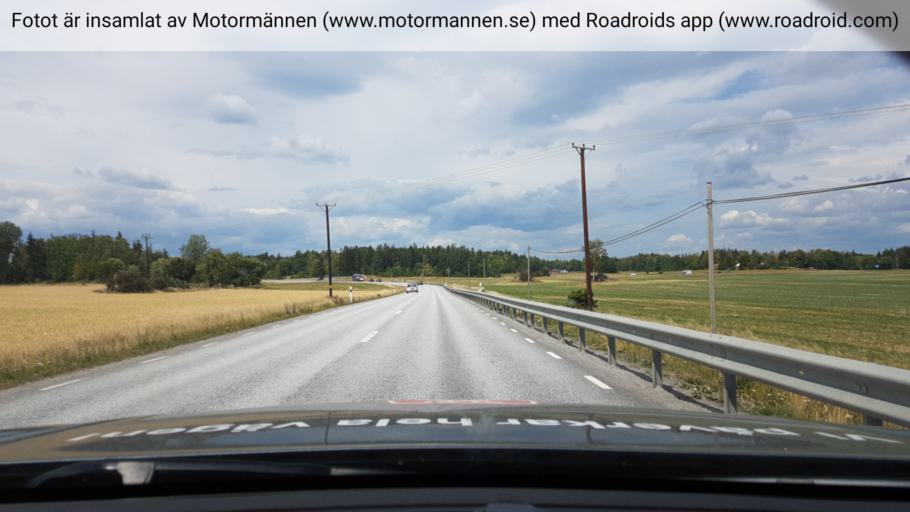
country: SE
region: Uppsala
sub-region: Habo Kommun
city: Balsta
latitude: 59.6277
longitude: 17.6018
